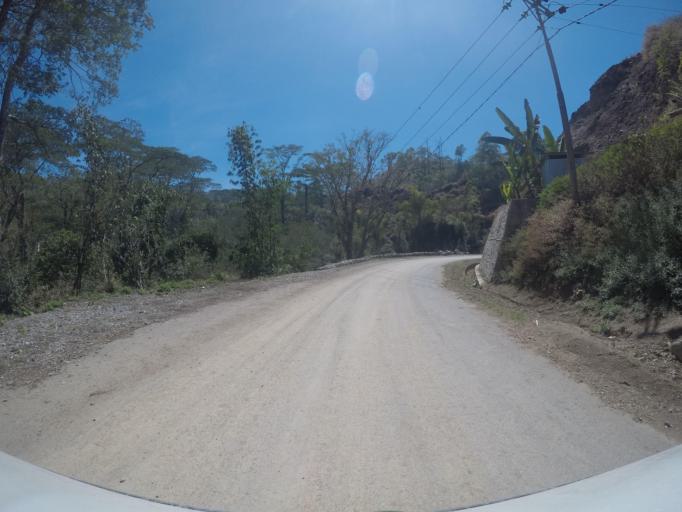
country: TL
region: Ermera
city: Gleno
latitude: -8.7895
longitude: 125.3775
